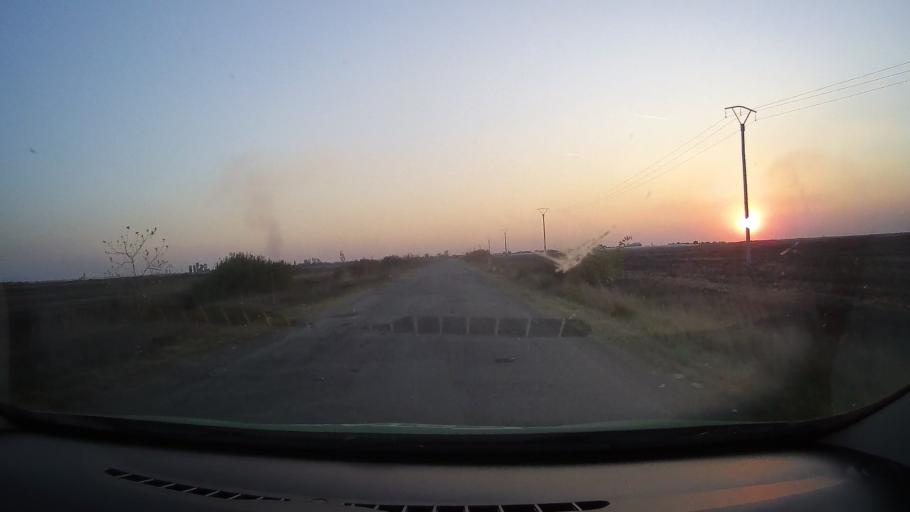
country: RO
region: Arad
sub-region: Comuna Olari
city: Olari
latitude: 46.3975
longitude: 21.5615
